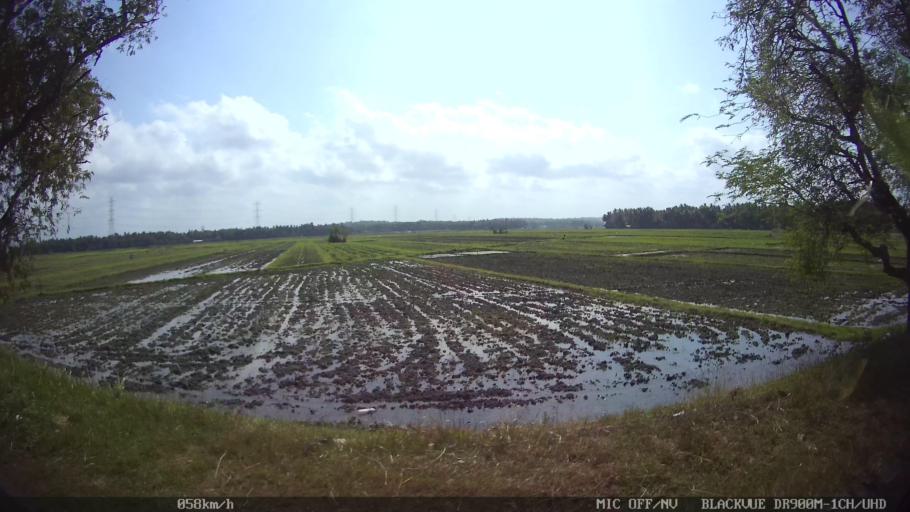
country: ID
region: Daerah Istimewa Yogyakarta
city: Srandakan
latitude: -7.9232
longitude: 110.1861
